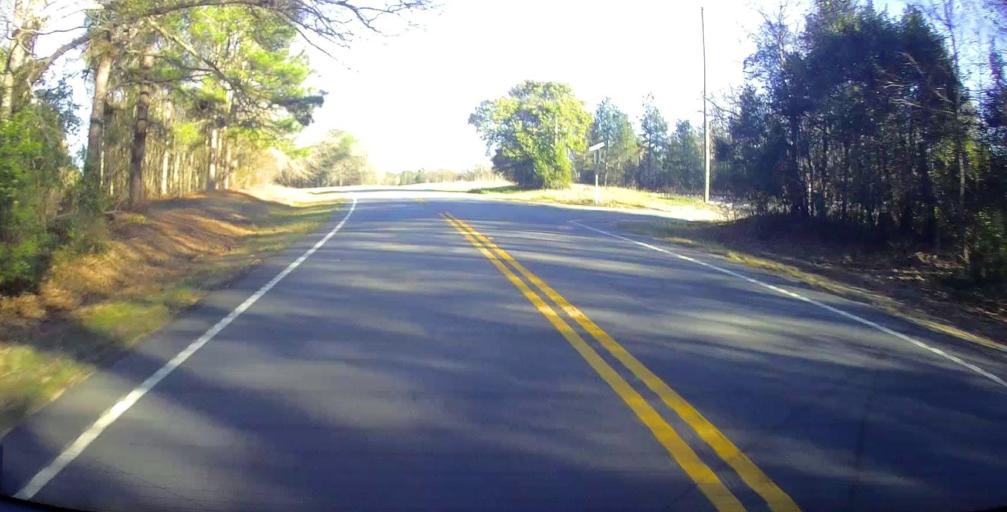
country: US
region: Georgia
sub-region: Taylor County
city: Butler
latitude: 32.4759
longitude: -84.3866
